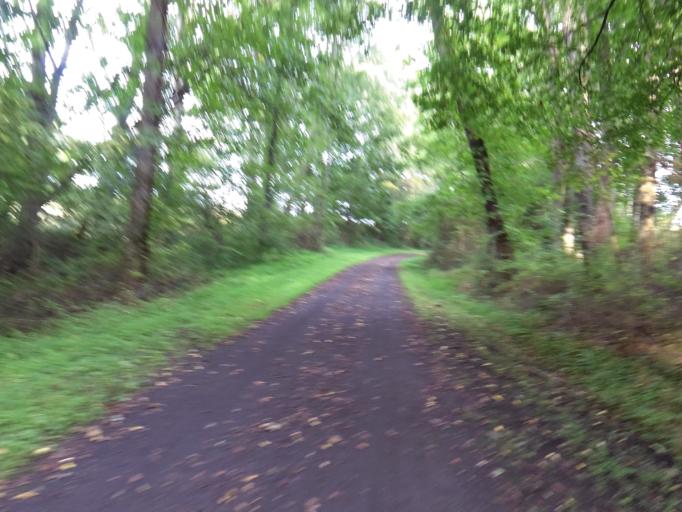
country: US
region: Virginia
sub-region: Washington County
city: Abingdon
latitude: 36.6800
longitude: -81.9402
